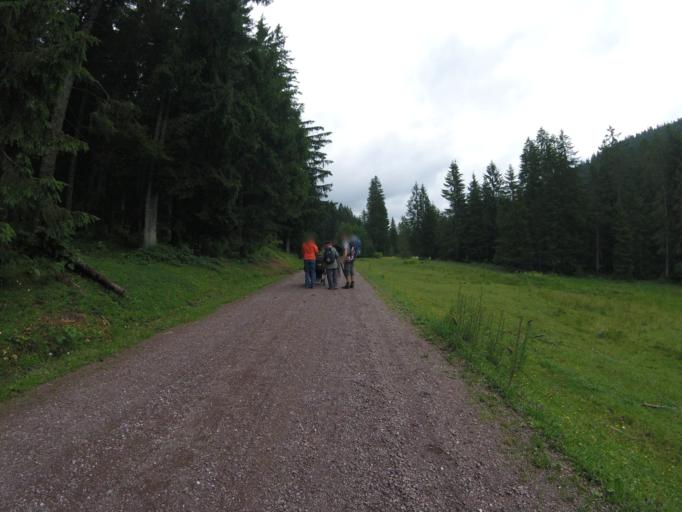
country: AT
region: Tyrol
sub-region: Politischer Bezirk Kitzbuhel
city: Waidring
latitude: 47.6531
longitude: 12.6043
